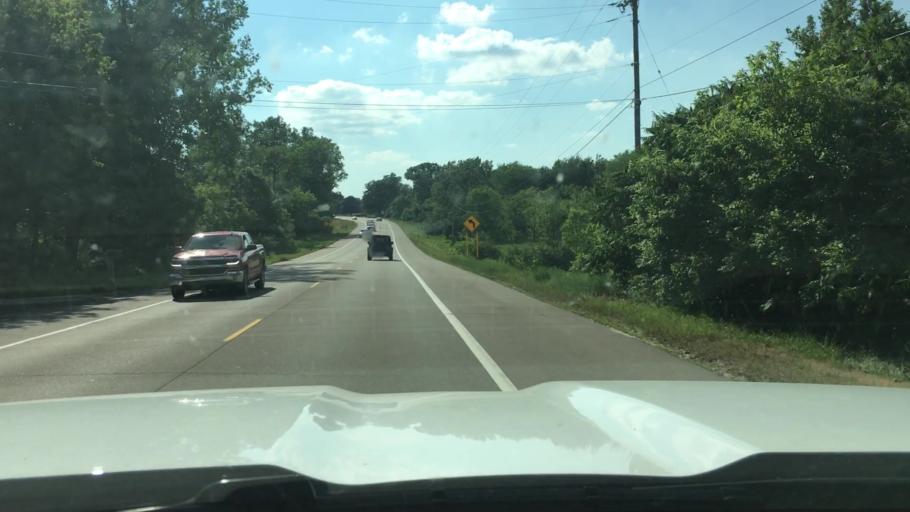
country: US
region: Michigan
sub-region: Kent County
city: Rockford
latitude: 43.0856
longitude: -85.4651
